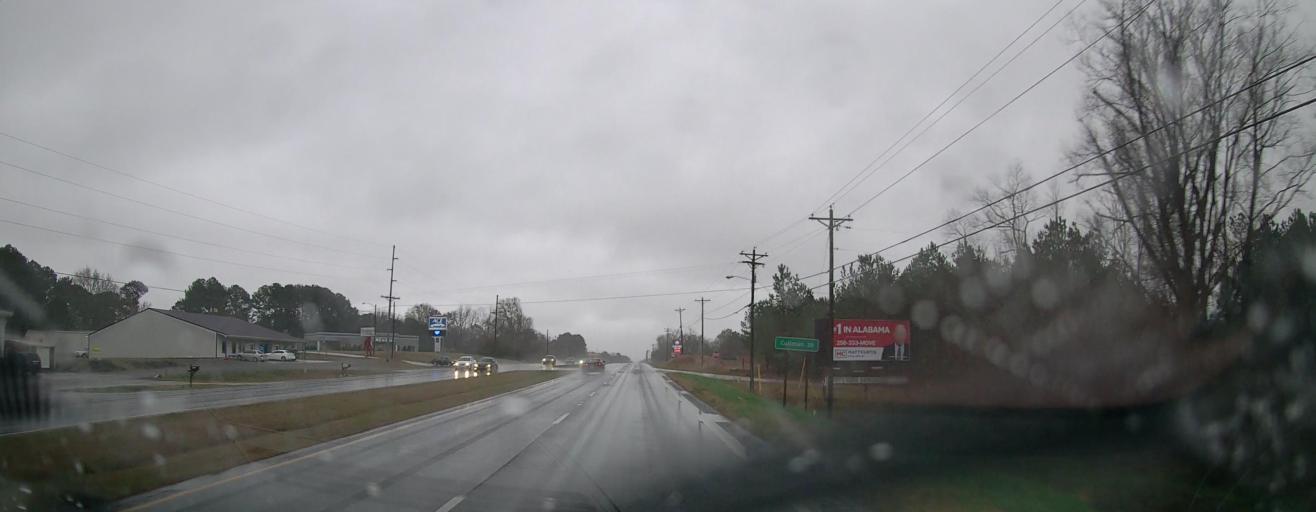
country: US
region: Alabama
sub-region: Morgan County
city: Hartselle
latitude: 34.4689
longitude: -86.9558
